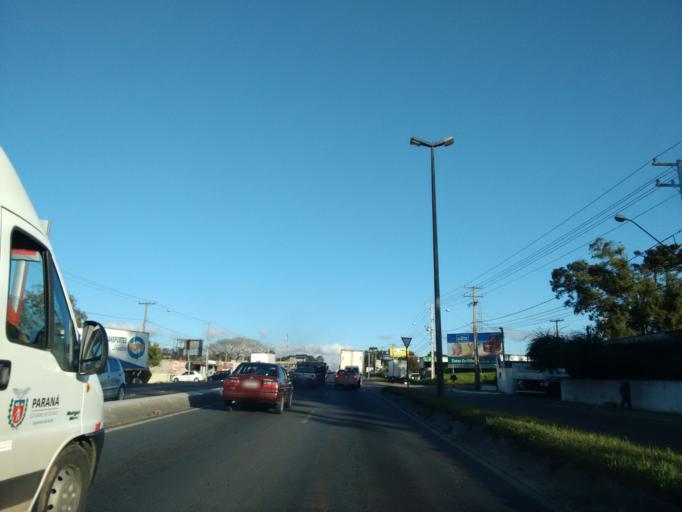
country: BR
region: Parana
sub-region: Sao Jose Dos Pinhais
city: Sao Jose dos Pinhais
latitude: -25.5595
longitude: -49.1851
